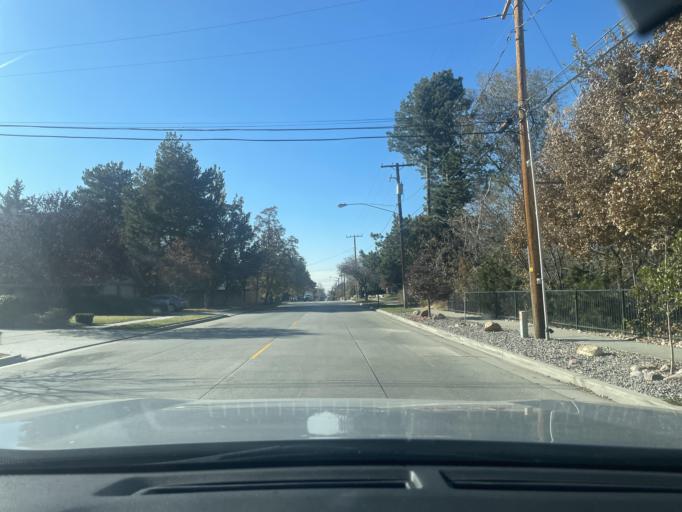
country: US
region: Utah
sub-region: Salt Lake County
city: Willard
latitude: 40.7417
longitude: -111.8318
